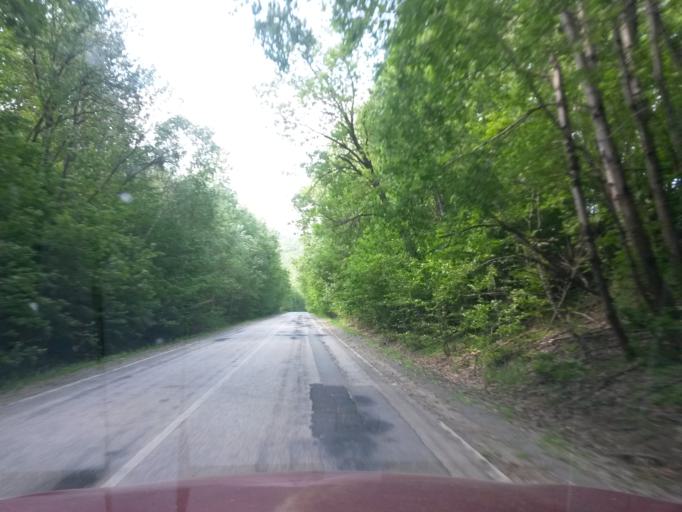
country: SK
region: Kosicky
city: Moldava nad Bodvou
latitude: 48.7296
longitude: 21.0868
